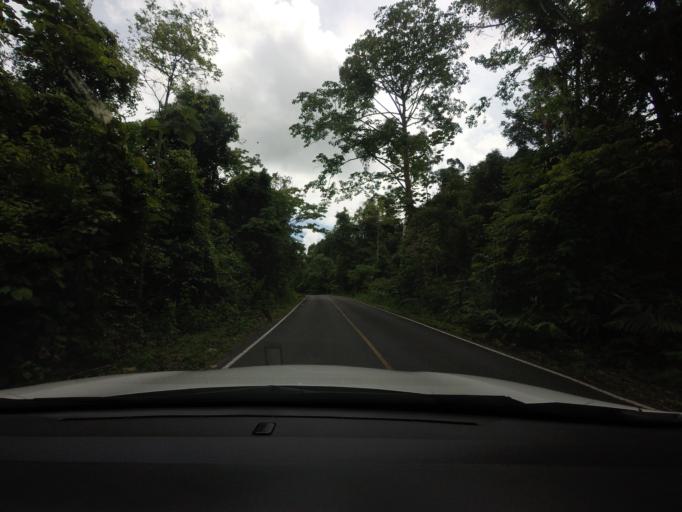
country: TH
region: Nakhon Nayok
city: Pak Phli
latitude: 14.2795
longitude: 101.3928
